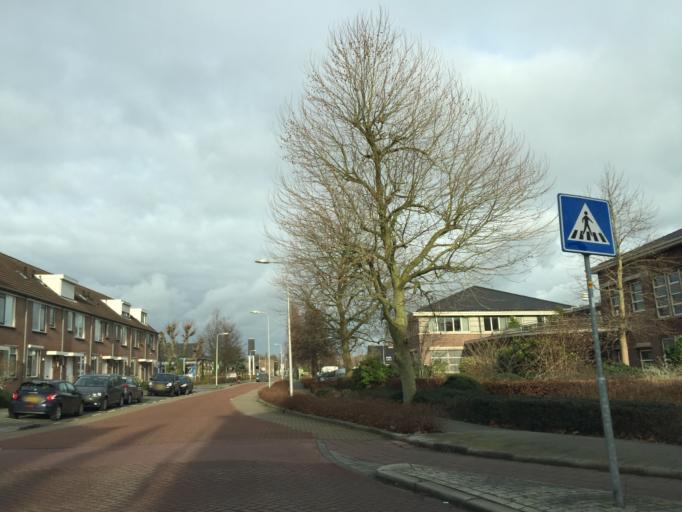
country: NL
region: South Holland
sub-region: Gemeente Boskoop
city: Boskoop
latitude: 52.0744
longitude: 4.6640
